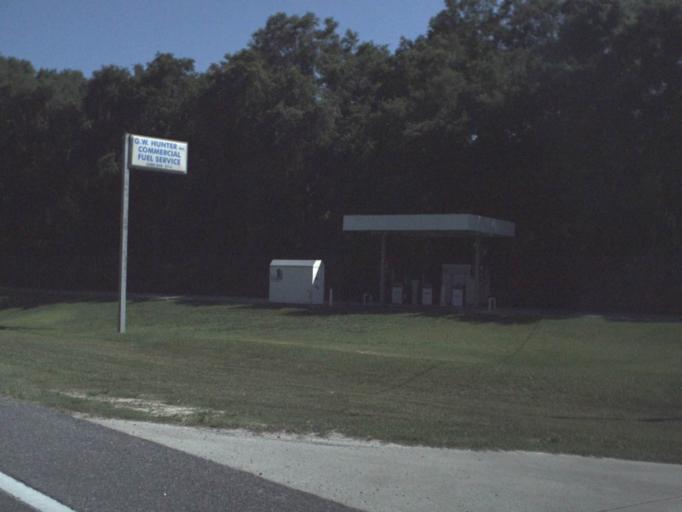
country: US
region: Florida
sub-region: Alachua County
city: High Springs
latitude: 29.9178
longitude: -82.7086
